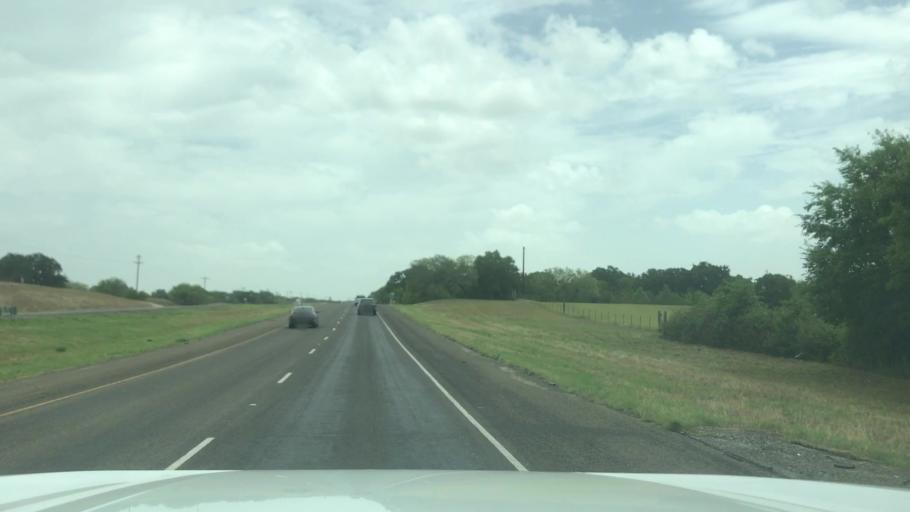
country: US
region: Texas
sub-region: McLennan County
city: Riesel
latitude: 31.5022
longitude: -96.9414
